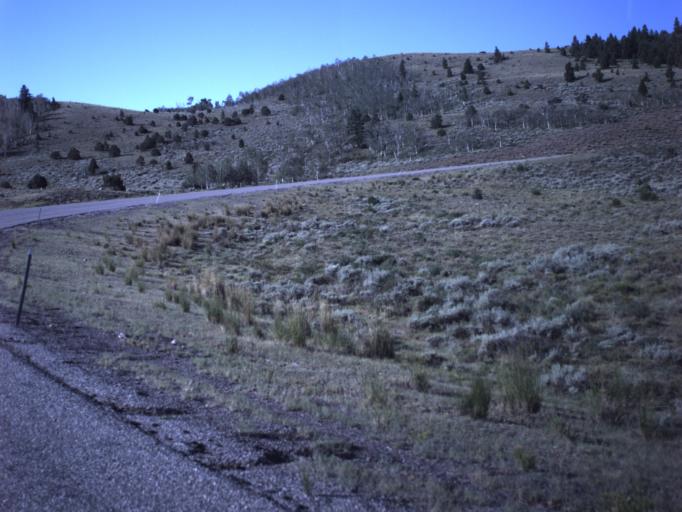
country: US
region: Utah
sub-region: Wayne County
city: Loa
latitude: 38.6014
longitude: -111.4607
